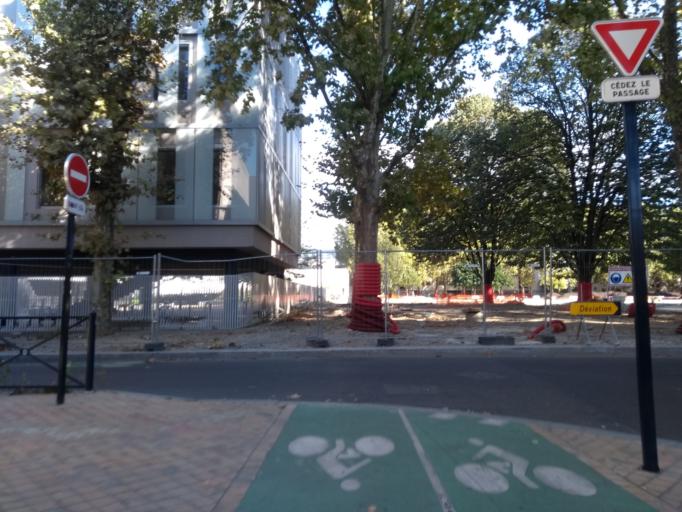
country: FR
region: Aquitaine
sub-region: Departement de la Gironde
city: Bordeaux
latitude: 44.8299
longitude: -0.5632
